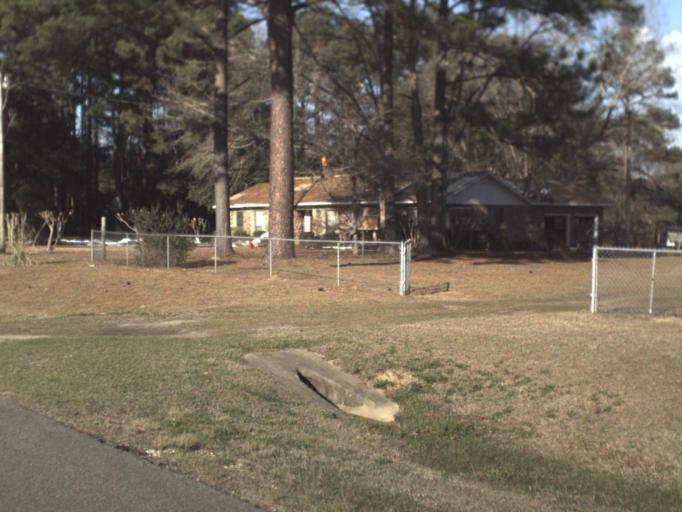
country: US
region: Florida
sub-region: Jackson County
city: Marianna
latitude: 30.7132
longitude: -85.2307
